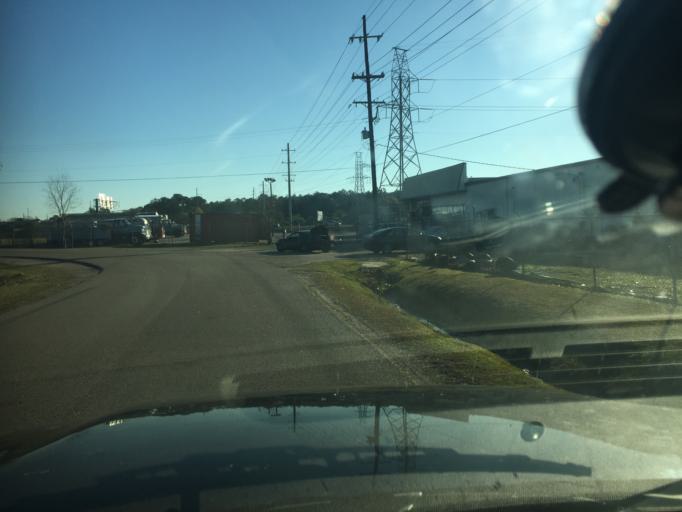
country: US
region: Louisiana
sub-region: Saint Tammany Parish
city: Slidell
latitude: 30.2514
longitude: -89.7640
